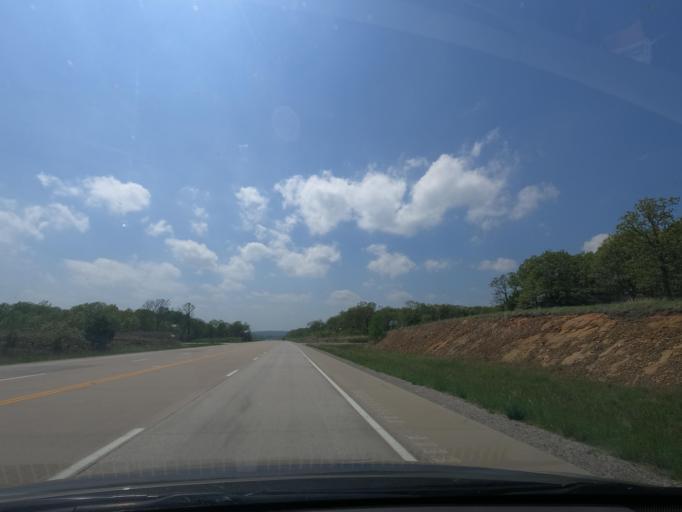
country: US
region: Kansas
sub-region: Wilson County
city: Fredonia
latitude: 37.6142
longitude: -95.9187
